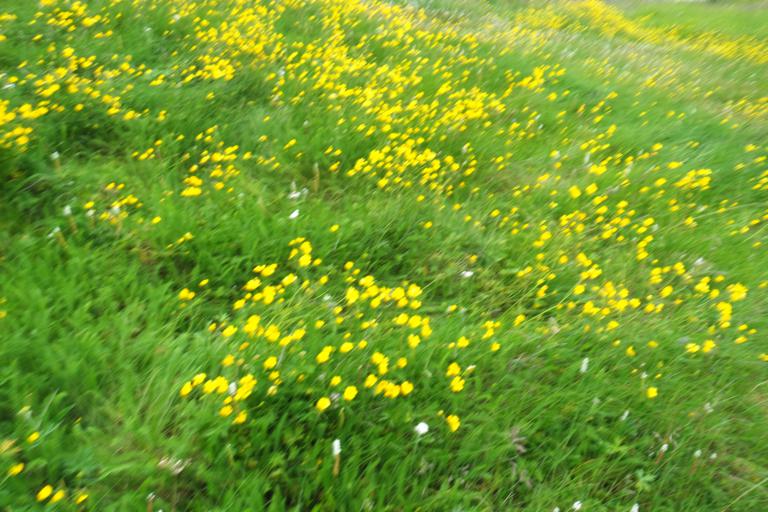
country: NO
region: Finnmark Fylke
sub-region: Porsanger
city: Lakselv
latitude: 70.2999
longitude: 25.1676
